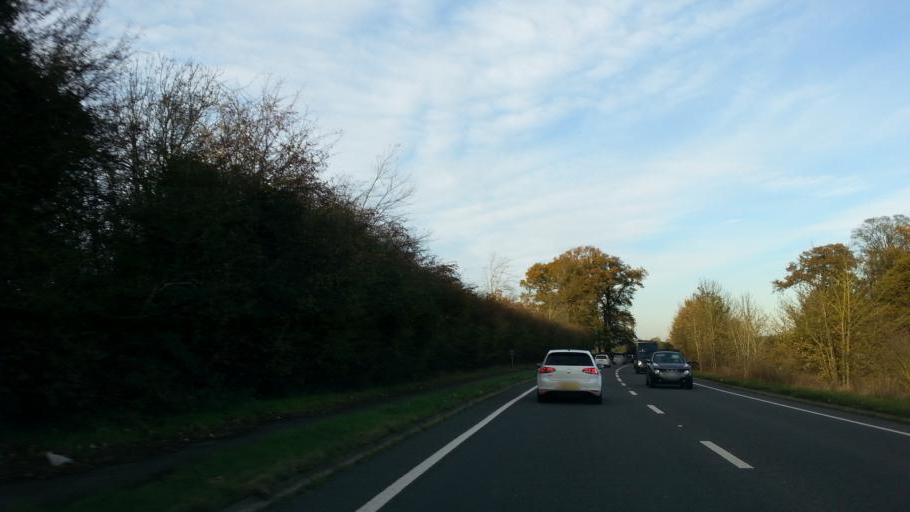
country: GB
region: England
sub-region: Northamptonshire
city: Broughton
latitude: 52.3752
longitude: -0.7831
